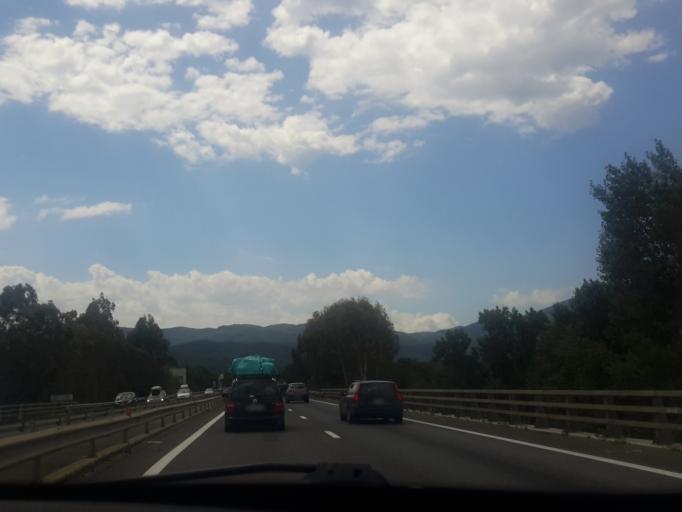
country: FR
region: Languedoc-Roussillon
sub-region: Departement des Pyrenees-Orientales
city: el Volo
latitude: 42.5171
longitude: 2.8187
